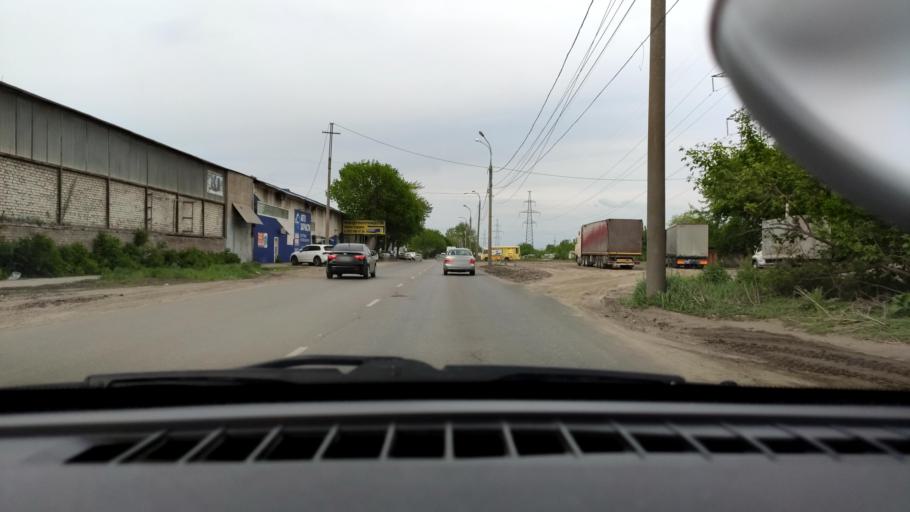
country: RU
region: Samara
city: Smyshlyayevka
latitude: 53.2271
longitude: 50.3022
